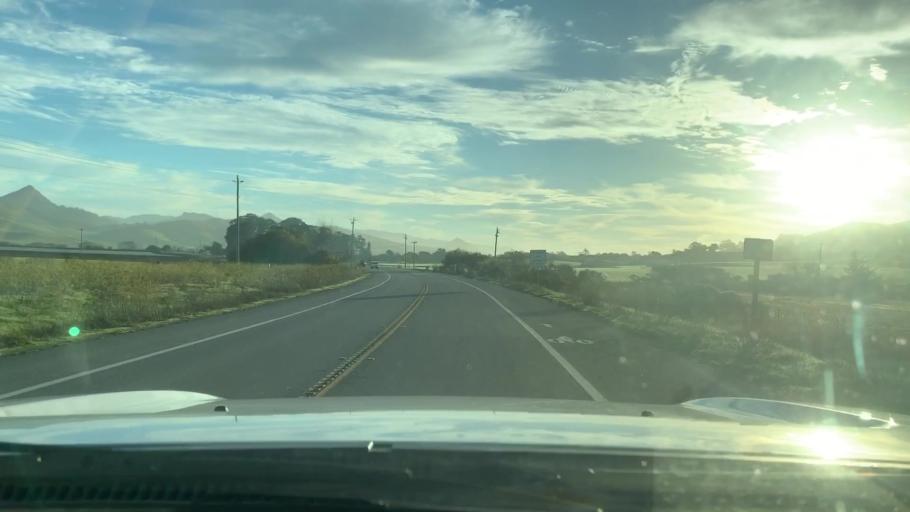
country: US
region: California
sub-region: San Luis Obispo County
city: Los Osos
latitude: 35.2988
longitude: -120.7853
